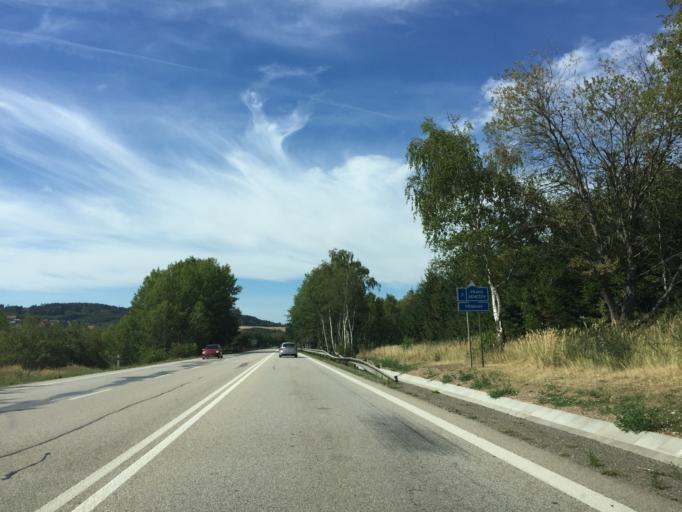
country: CZ
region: Central Bohemia
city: Votice
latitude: 49.6410
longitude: 14.6477
